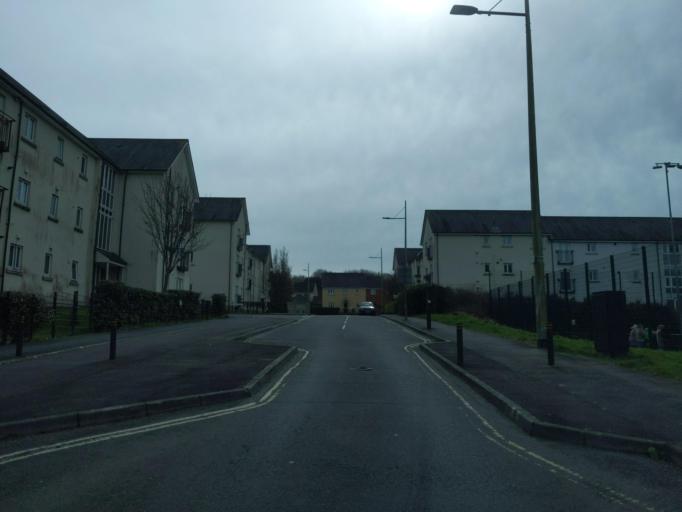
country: GB
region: England
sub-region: Plymouth
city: Plymouth
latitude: 50.4094
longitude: -4.1428
